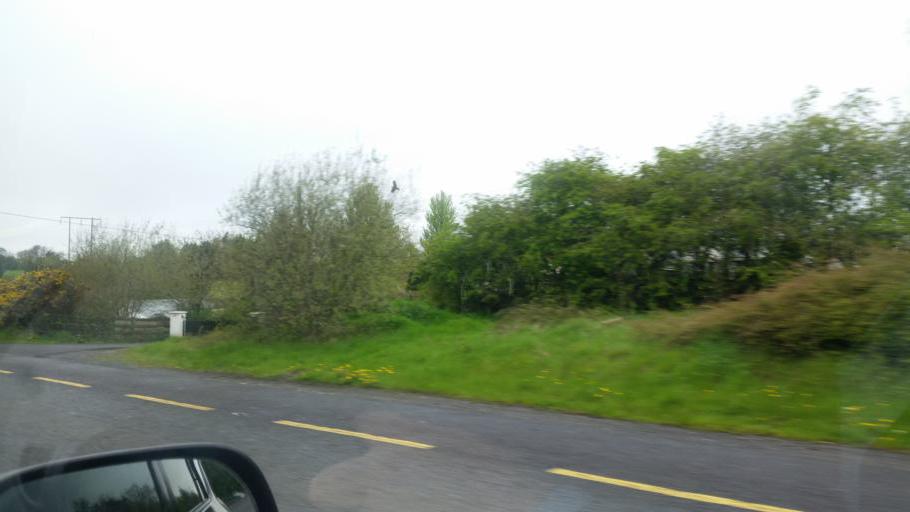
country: IE
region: Leinster
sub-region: Laois
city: Portlaoise
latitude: 53.0488
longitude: -7.2435
